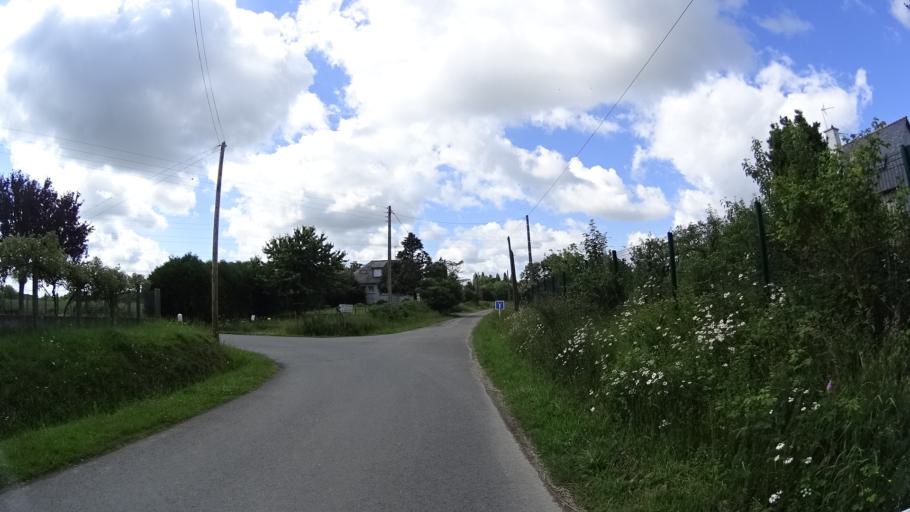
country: FR
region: Brittany
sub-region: Departement d'Ille-et-Vilaine
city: Le Rheu
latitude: 48.1165
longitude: -1.8055
